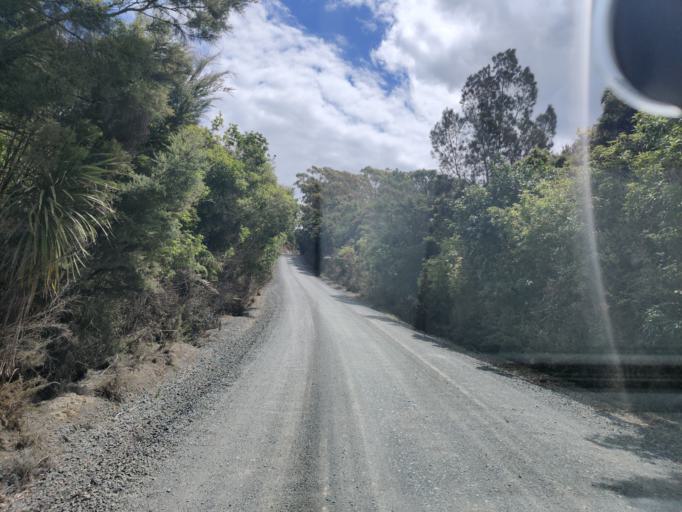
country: NZ
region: Northland
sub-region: Far North District
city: Paihia
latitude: -35.2594
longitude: 174.0604
